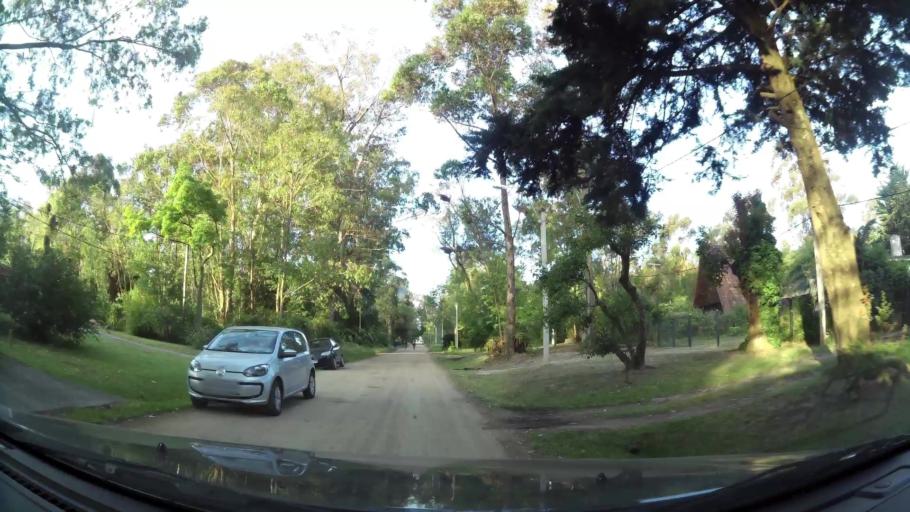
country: UY
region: Canelones
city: Atlantida
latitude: -34.7716
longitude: -55.8048
